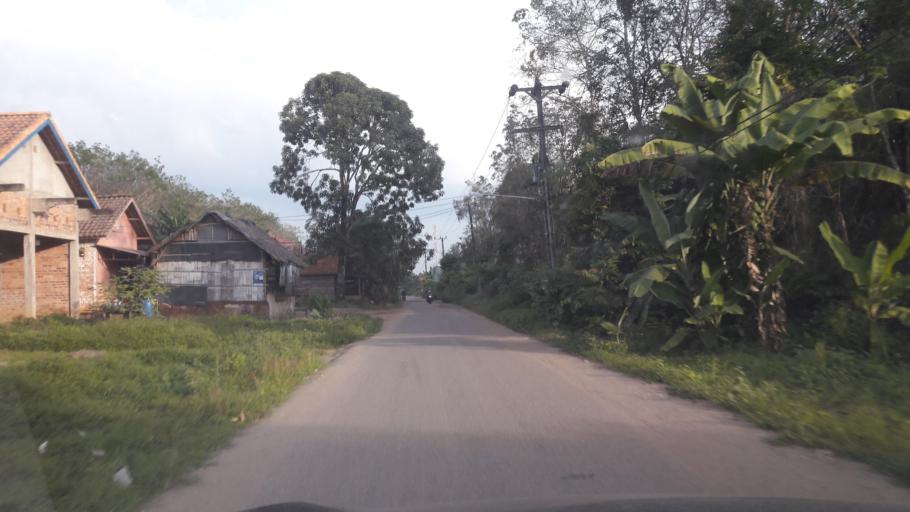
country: ID
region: South Sumatra
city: Gunungmenang
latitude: -3.3214
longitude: 104.0939
